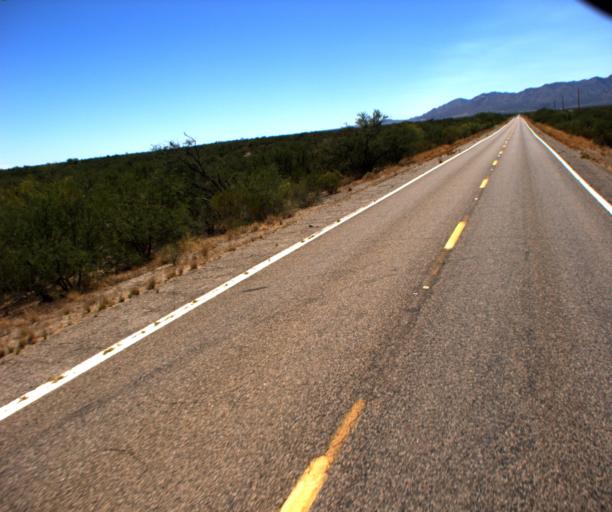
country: US
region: Arizona
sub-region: Pima County
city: Three Points
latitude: 31.8380
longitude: -111.4062
